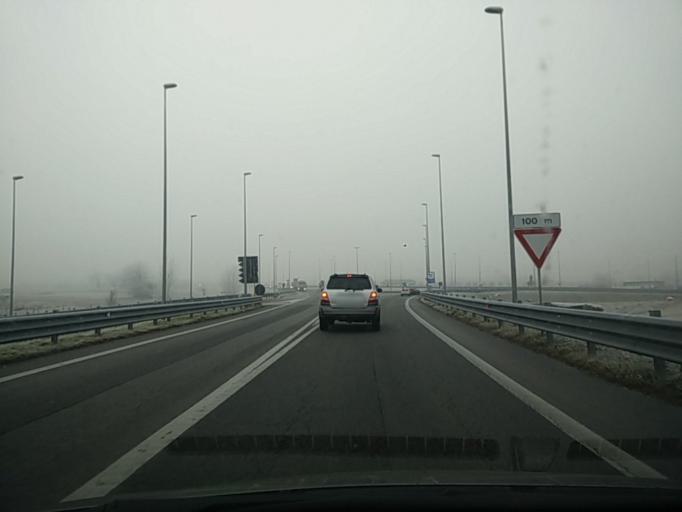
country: IT
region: Veneto
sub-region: Provincia di Belluno
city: Seren del Grappa
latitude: 46.0017
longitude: 11.8385
